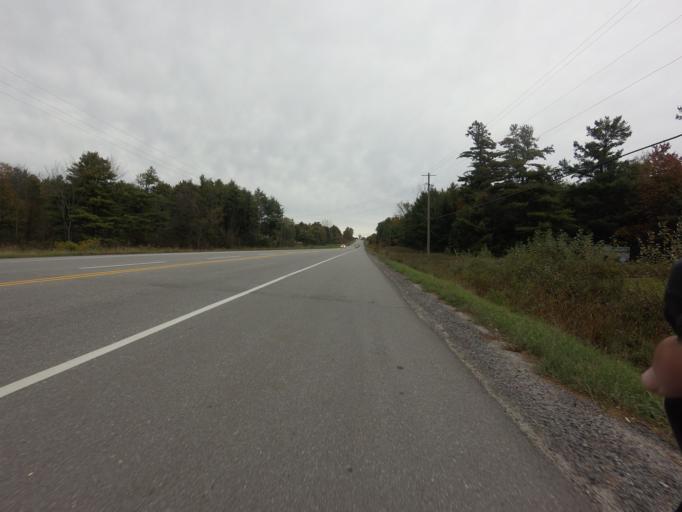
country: CA
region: Ontario
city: Gananoque
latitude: 44.4871
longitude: -76.1930
